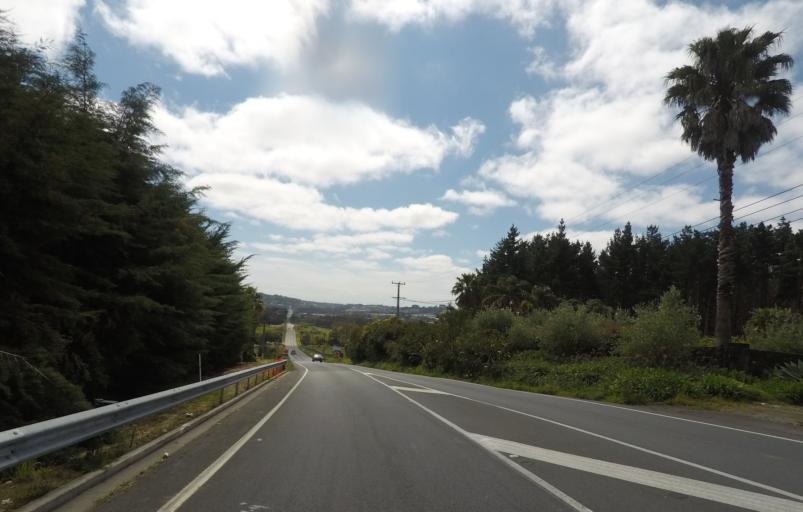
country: NZ
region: Auckland
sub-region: Auckland
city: Manukau City
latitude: -36.9891
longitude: 174.9184
